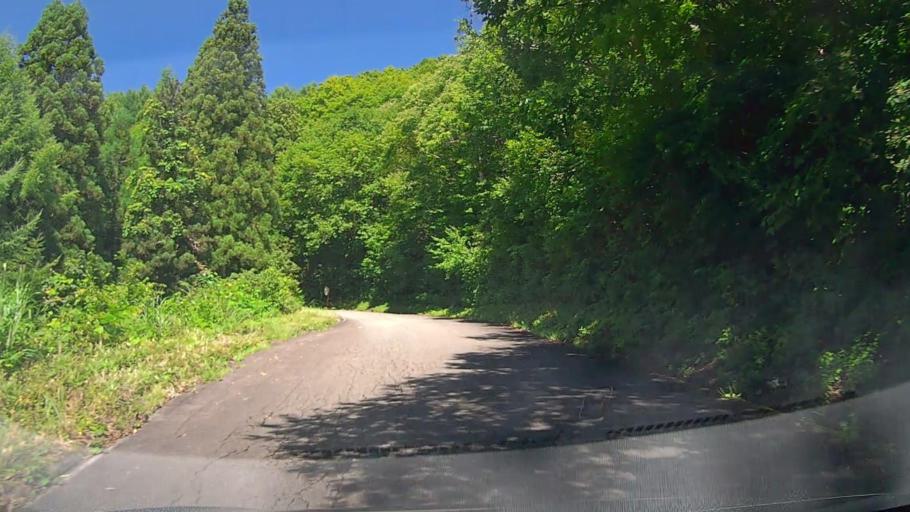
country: JP
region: Nagano
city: Iiyama
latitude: 36.9337
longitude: 138.4554
